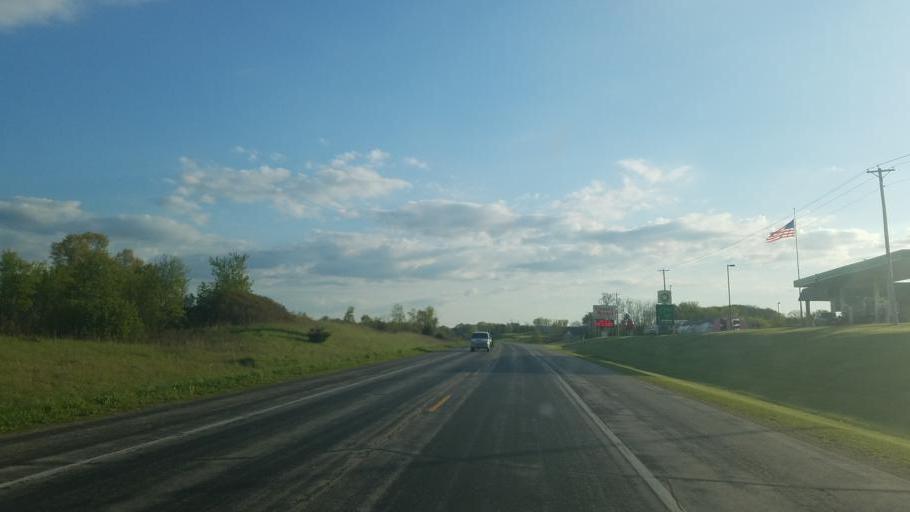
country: US
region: Wisconsin
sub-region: Vernon County
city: Hillsboro
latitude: 43.6614
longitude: -90.3261
